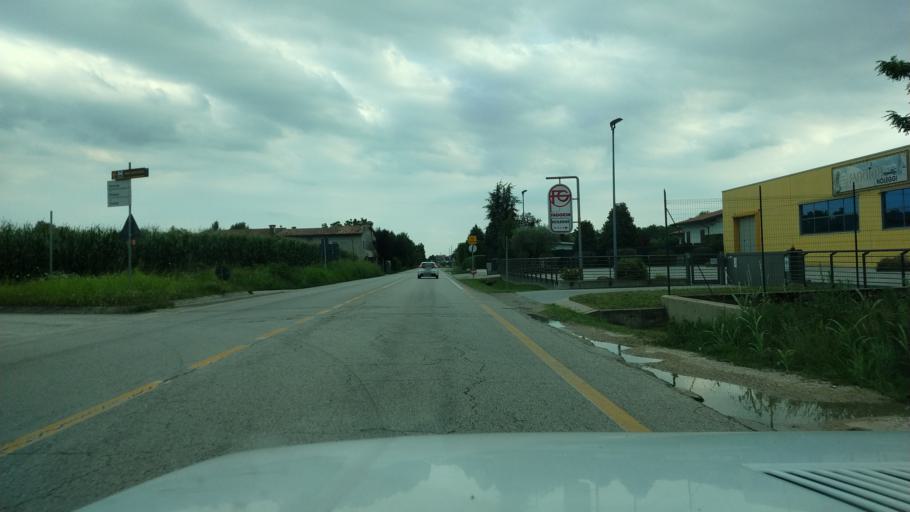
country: IT
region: Veneto
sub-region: Provincia di Vicenza
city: Marostica
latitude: 45.7237
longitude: 11.6512
